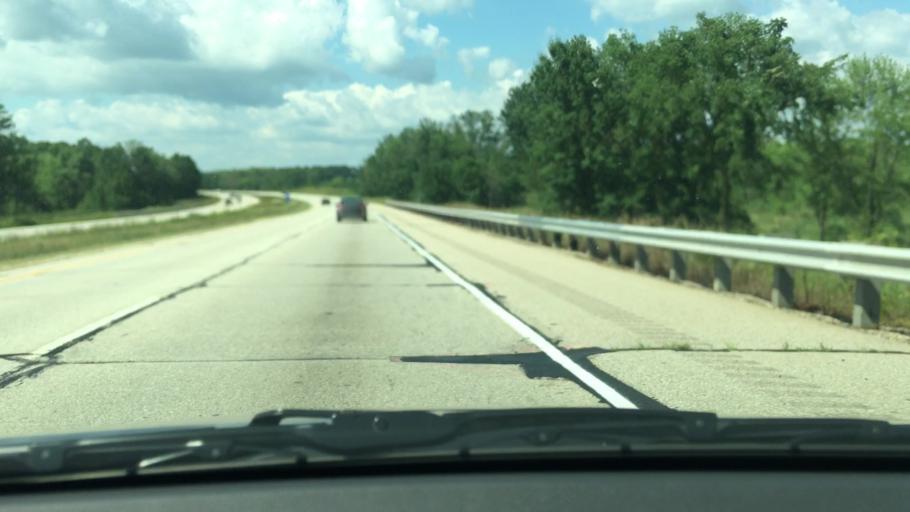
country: US
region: Wisconsin
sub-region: Dodge County
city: Theresa
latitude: 43.5006
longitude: -88.3667
